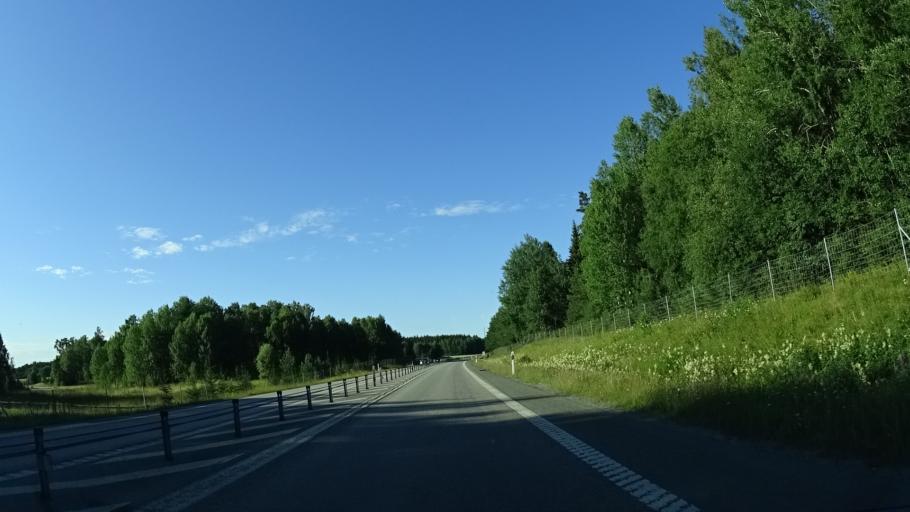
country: SE
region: Stockholm
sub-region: Vallentuna Kommun
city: Vallentuna
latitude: 59.5134
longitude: 18.1768
